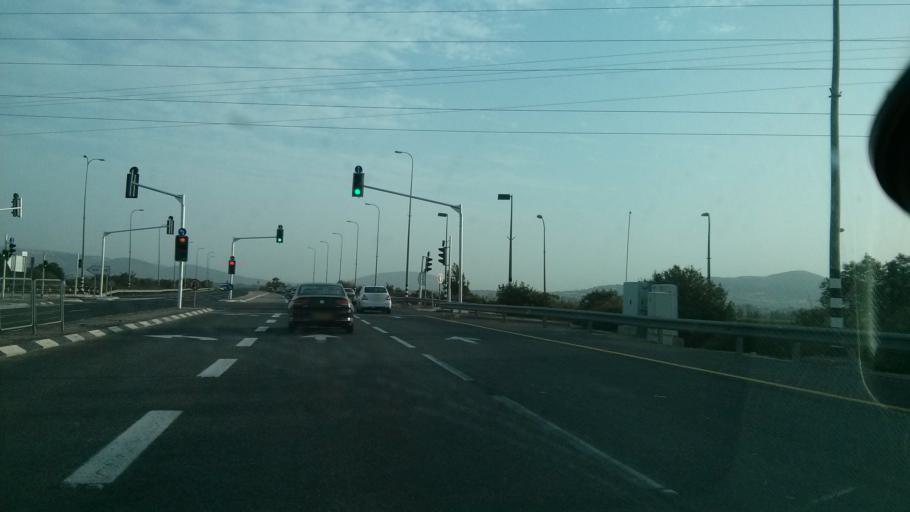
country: PS
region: West Bank
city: Zububah
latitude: 32.6003
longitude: 35.2599
